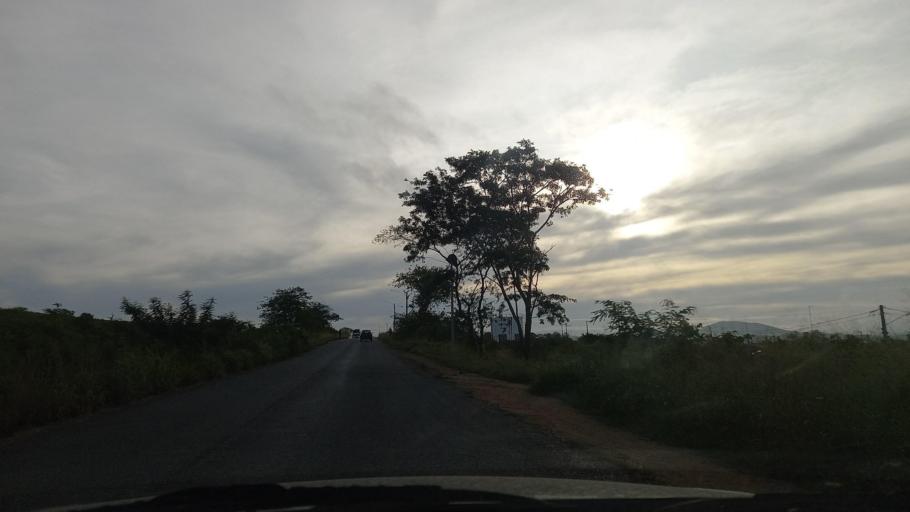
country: BR
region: Pernambuco
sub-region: Bezerros
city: Bezerros
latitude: -8.2151
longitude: -35.7435
